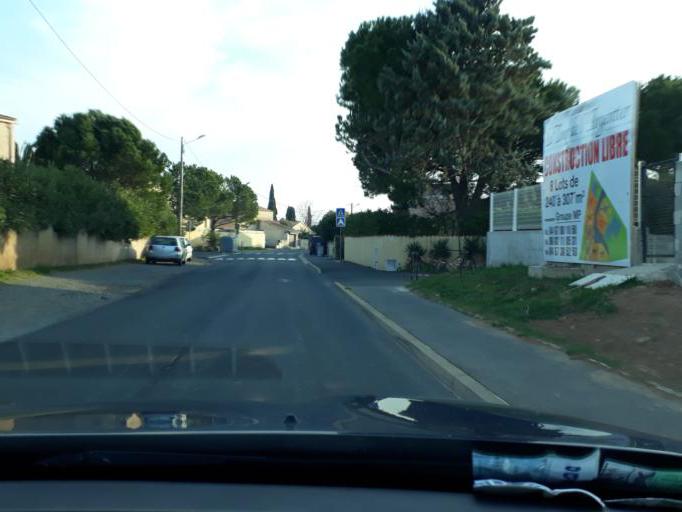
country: FR
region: Languedoc-Roussillon
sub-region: Departement de l'Herault
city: Marseillan
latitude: 43.3382
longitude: 3.5334
